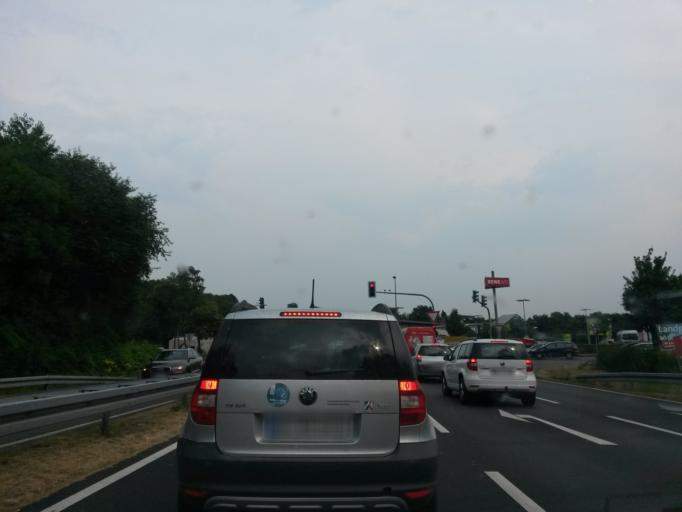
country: DE
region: North Rhine-Westphalia
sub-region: Regierungsbezirk Koln
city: Hennef
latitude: 50.7744
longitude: 7.3008
